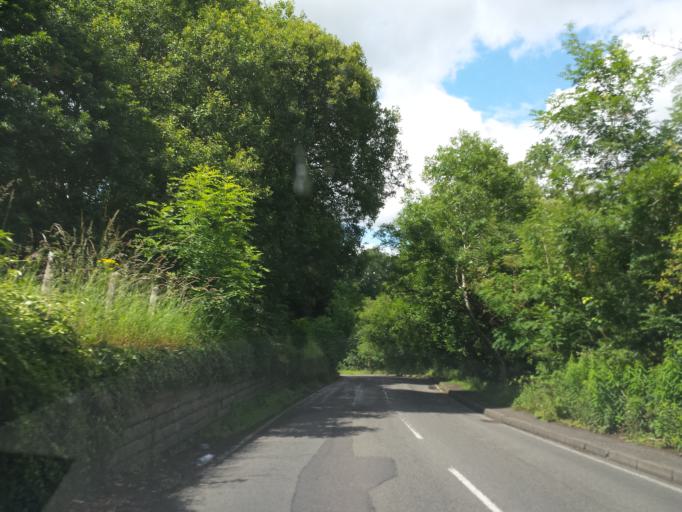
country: GB
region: Scotland
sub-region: Midlothian
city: Loanhead
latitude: 55.8516
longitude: -3.1637
